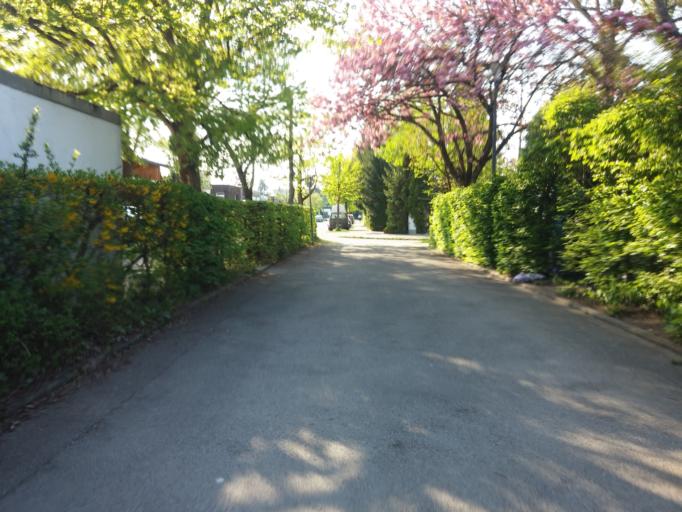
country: DE
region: Bavaria
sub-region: Upper Bavaria
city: Neubiberg
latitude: 48.1037
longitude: 11.6653
